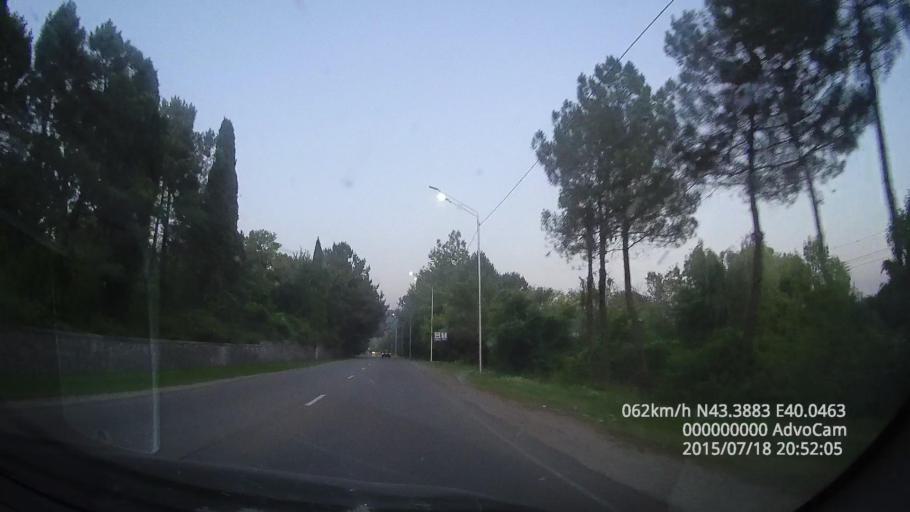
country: GE
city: Gantiadi
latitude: 43.3881
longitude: 40.0478
